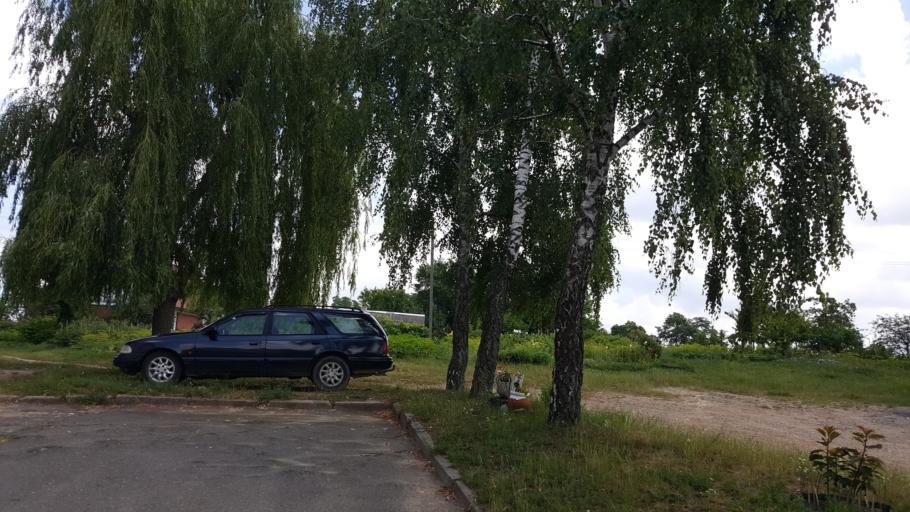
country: BY
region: Brest
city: Kamyanyets
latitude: 52.4016
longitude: 23.8227
